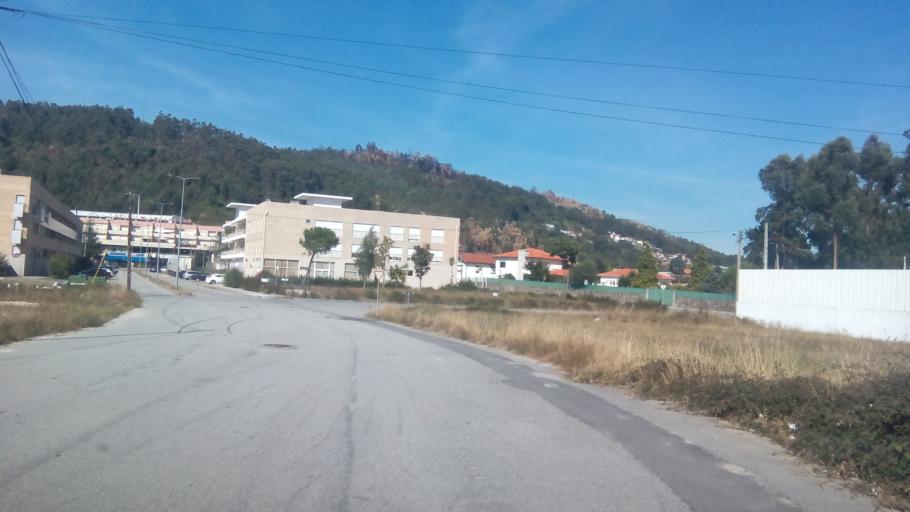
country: PT
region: Porto
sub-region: Paredes
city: Baltar
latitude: 41.1884
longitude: -8.3972
